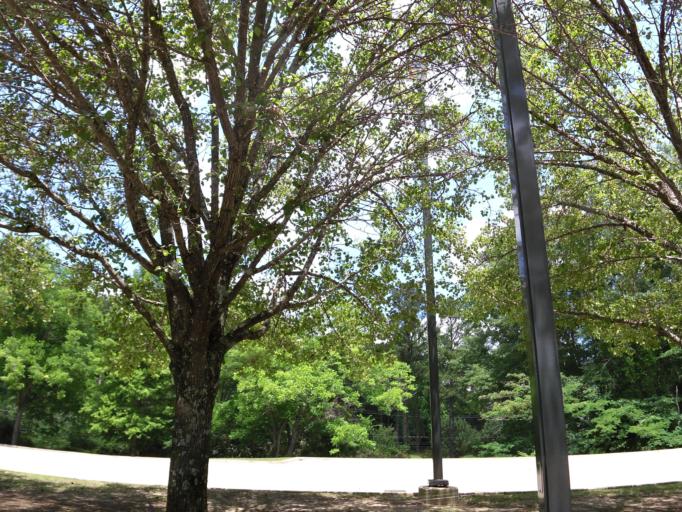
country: US
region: Mississippi
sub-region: Lee County
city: Tupelo
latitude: 34.2602
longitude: -88.6794
